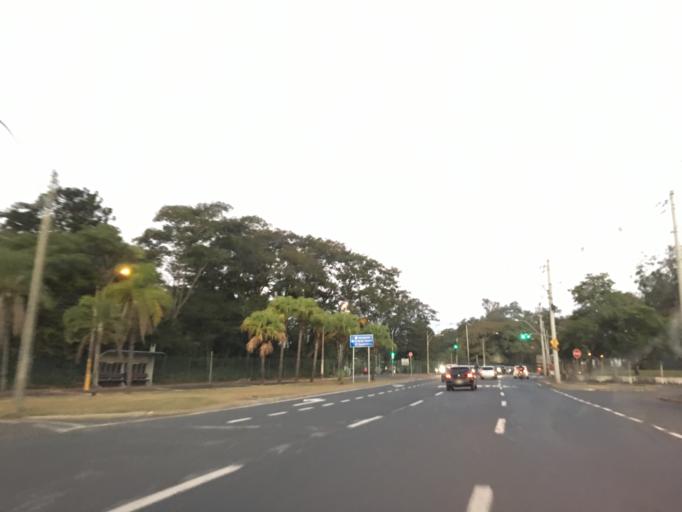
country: BR
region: Sao Paulo
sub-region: Piracicaba
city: Piracicaba
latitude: -22.7127
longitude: -47.6343
